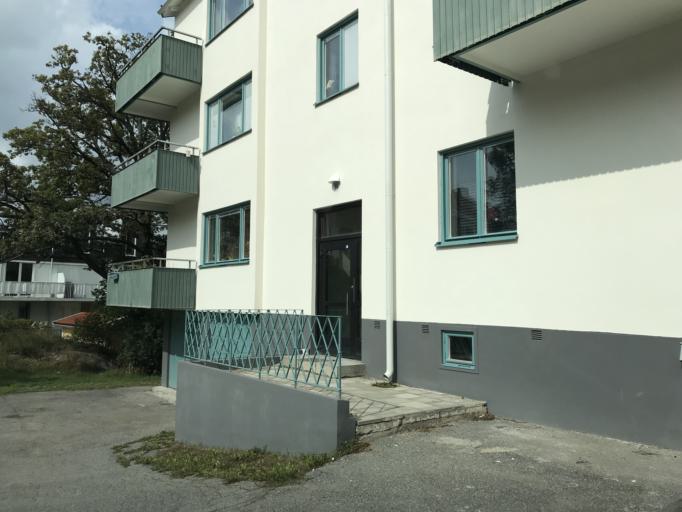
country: SE
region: Stockholm
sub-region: Sundbybergs Kommun
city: Sundbyberg
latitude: 59.3366
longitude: 17.9750
